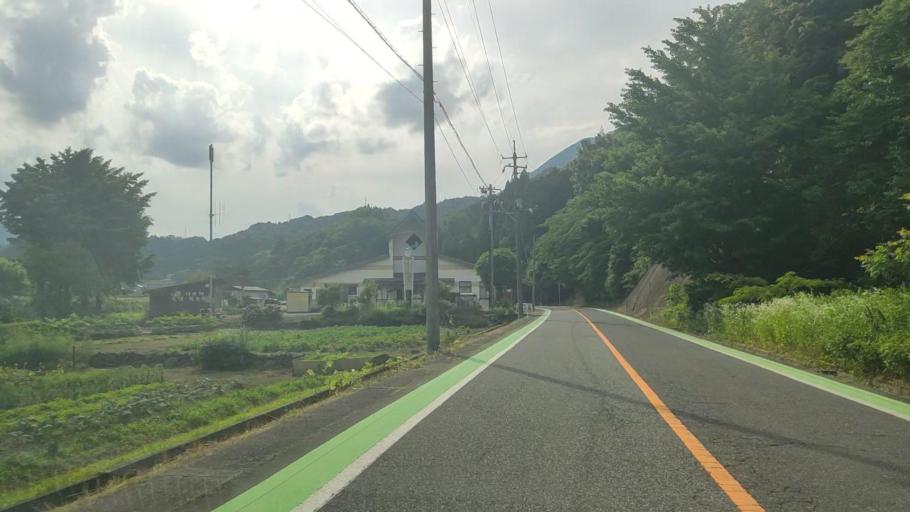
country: JP
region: Tottori
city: Tottori
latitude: 35.3306
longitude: 134.1066
